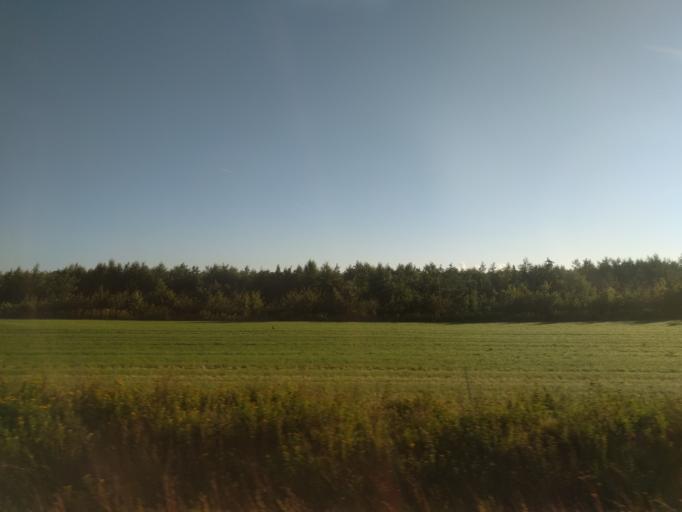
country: DK
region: South Denmark
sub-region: Nyborg Kommune
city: Nyborg
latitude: 55.3339
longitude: 10.7563
